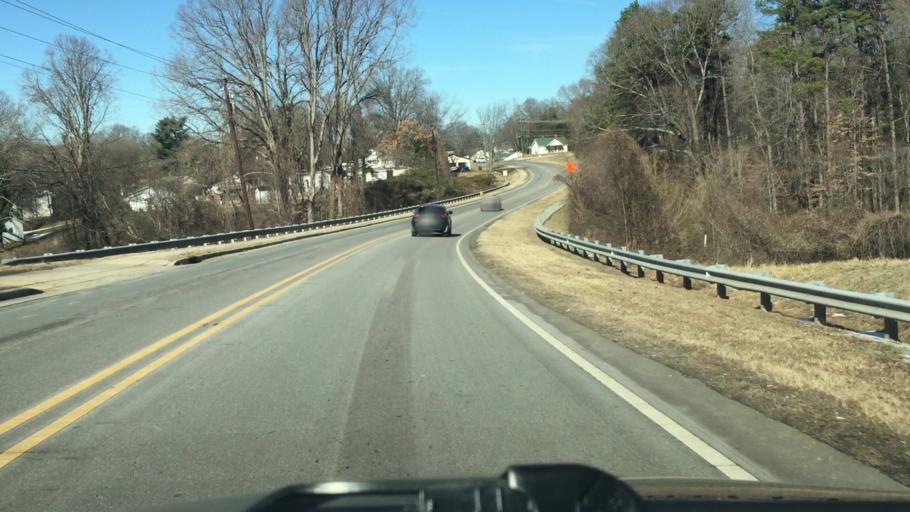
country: US
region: North Carolina
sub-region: Iredell County
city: Mooresville
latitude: 35.5870
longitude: -80.8124
